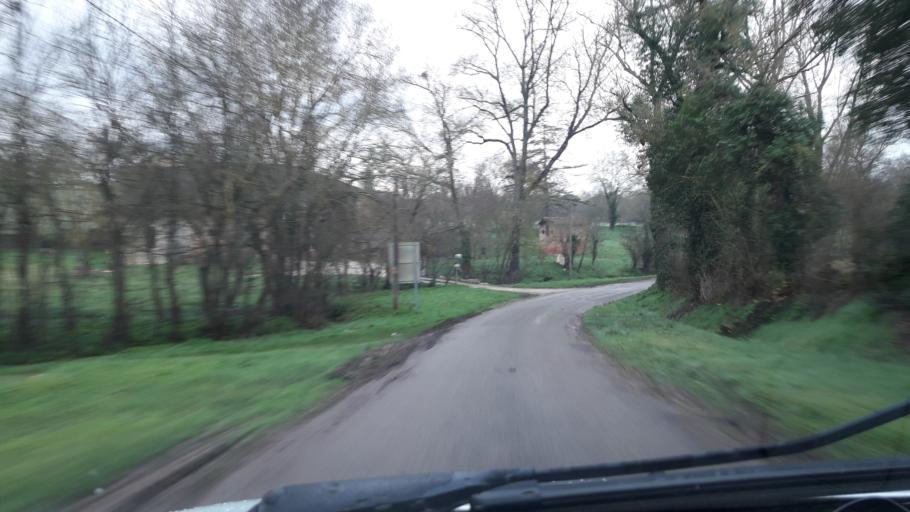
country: FR
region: Midi-Pyrenees
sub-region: Departement du Gers
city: Gimont
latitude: 43.6901
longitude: 0.9202
